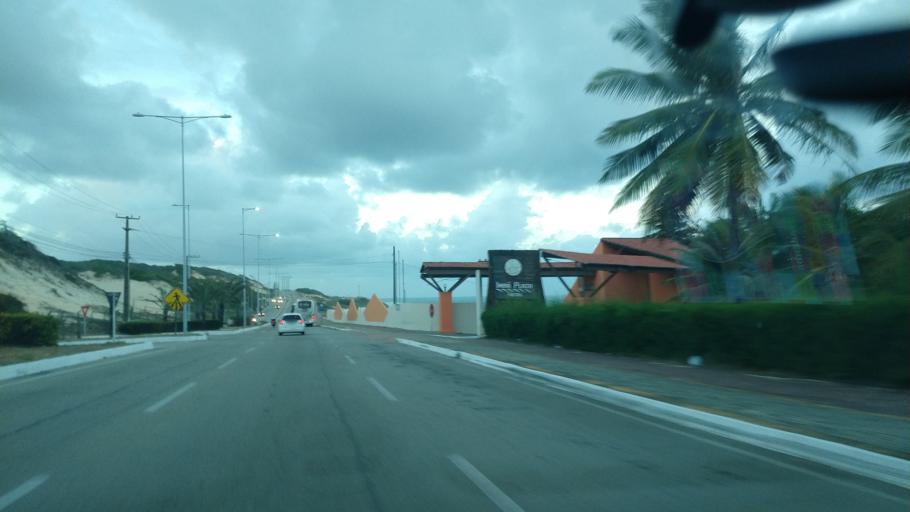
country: BR
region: Rio Grande do Norte
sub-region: Natal
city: Natal
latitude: -5.8274
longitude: -35.1832
